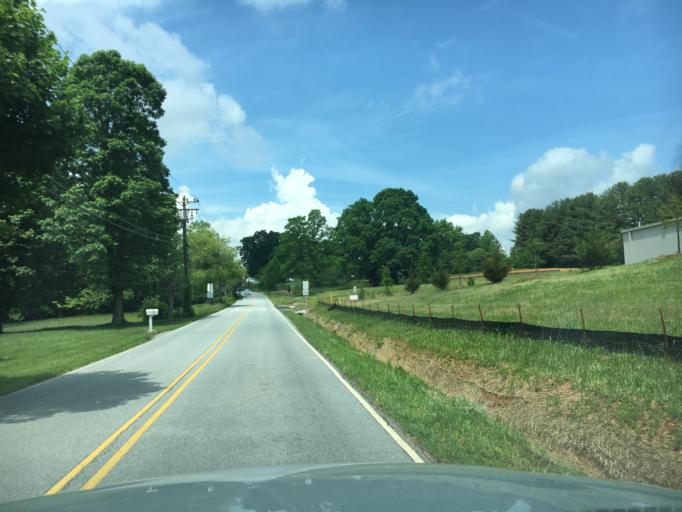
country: US
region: North Carolina
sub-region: Henderson County
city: Mills River
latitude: 35.3777
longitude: -82.5682
